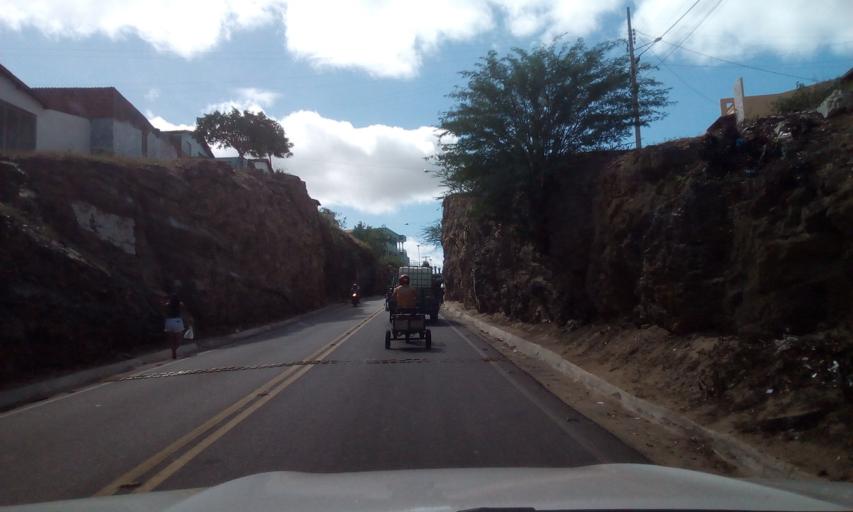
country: BR
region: Paraiba
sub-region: Picui
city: Picui
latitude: -6.5092
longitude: -36.3436
